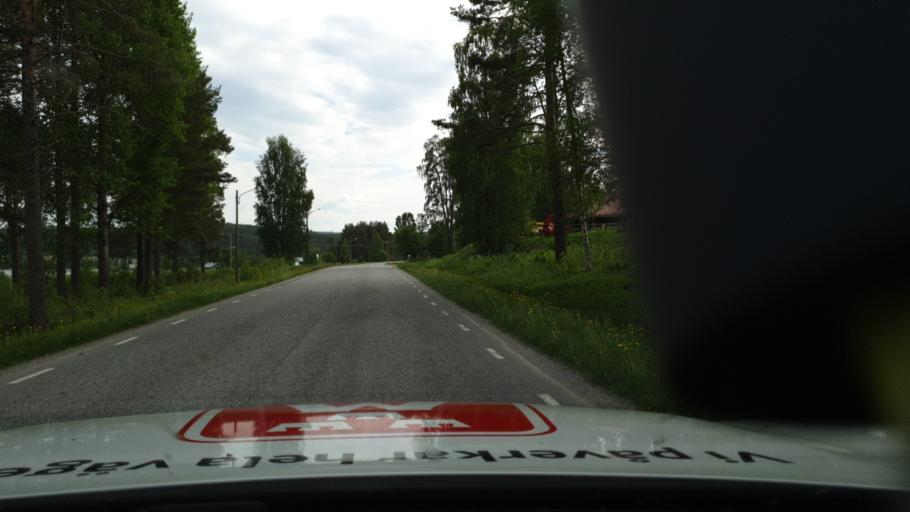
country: SE
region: Jaemtland
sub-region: Braecke Kommun
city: Braecke
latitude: 62.9770
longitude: 15.2015
